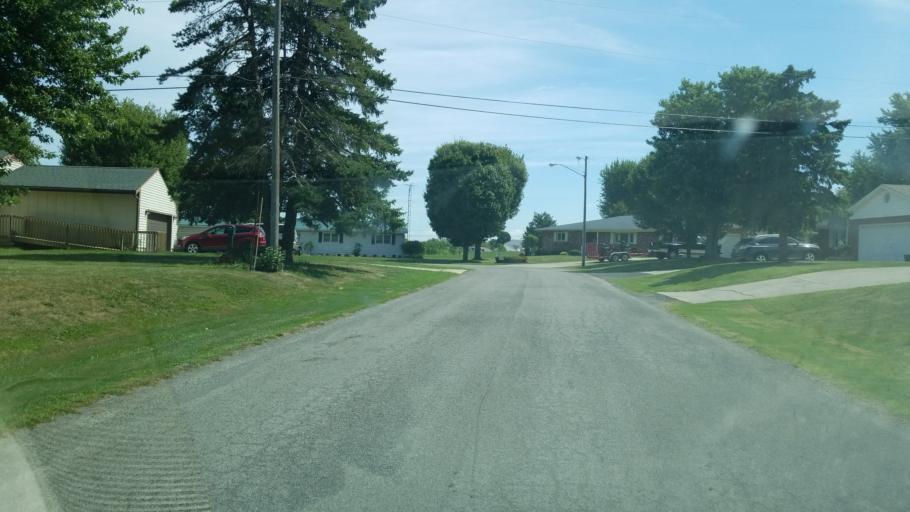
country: US
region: Ohio
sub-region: Hardin County
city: Kenton
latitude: 40.6605
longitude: -83.6011
